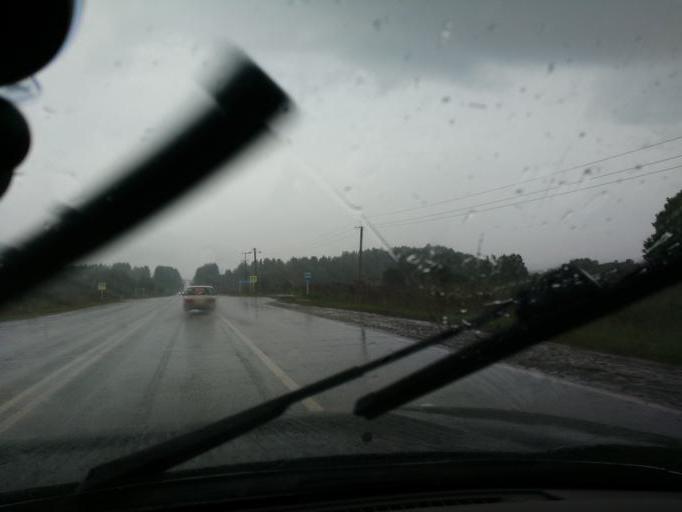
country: RU
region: Perm
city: Osa
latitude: 57.1562
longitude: 55.5299
